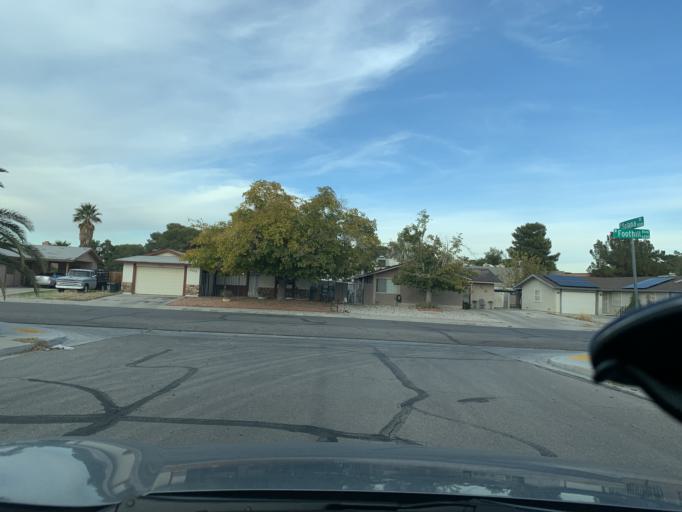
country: US
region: Nevada
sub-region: Clark County
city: Spring Valley
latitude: 36.0964
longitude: -115.2290
